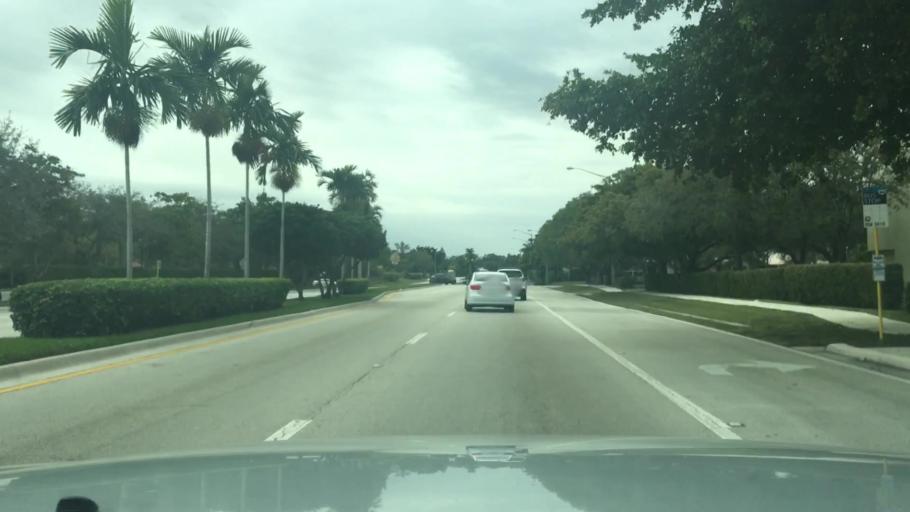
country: US
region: Florida
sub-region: Broward County
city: Margate
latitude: 26.2572
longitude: -80.2369
